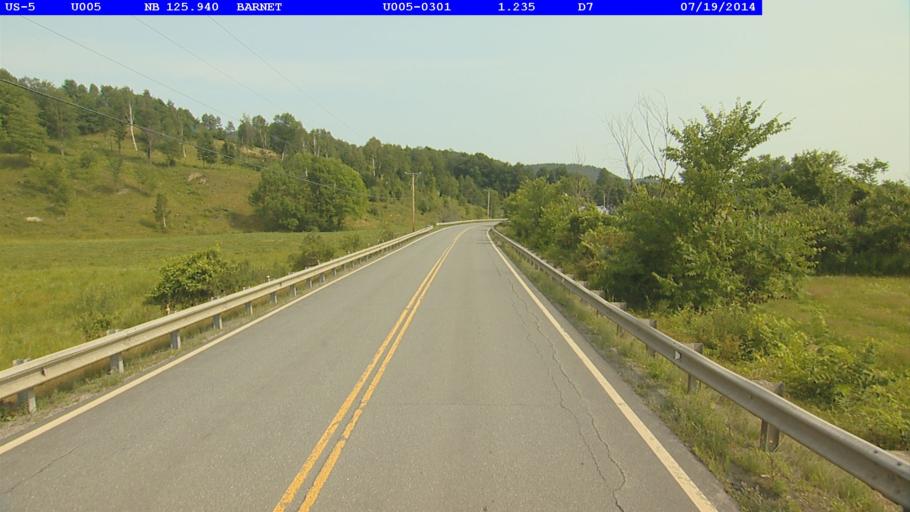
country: US
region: New Hampshire
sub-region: Grafton County
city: Woodsville
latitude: 44.2728
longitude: -72.0692
